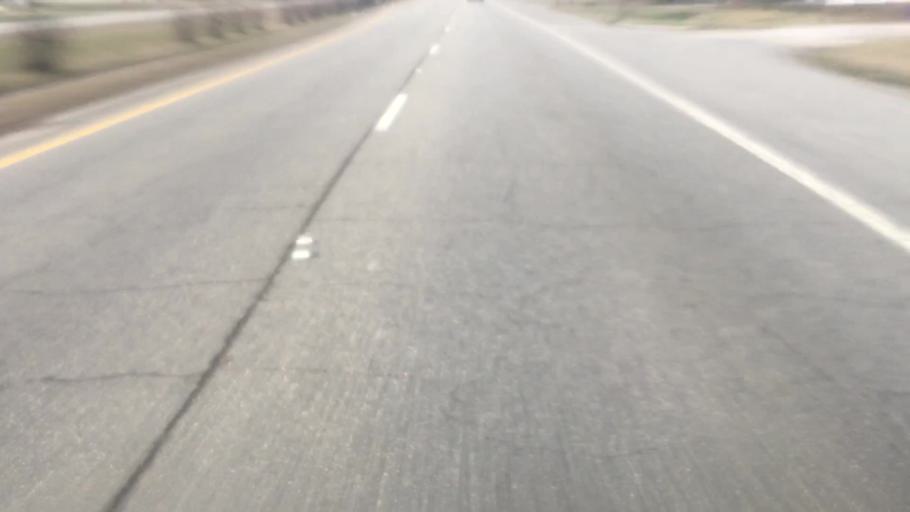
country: US
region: Alabama
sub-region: Walker County
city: Sumiton
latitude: 33.7412
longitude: -87.0375
